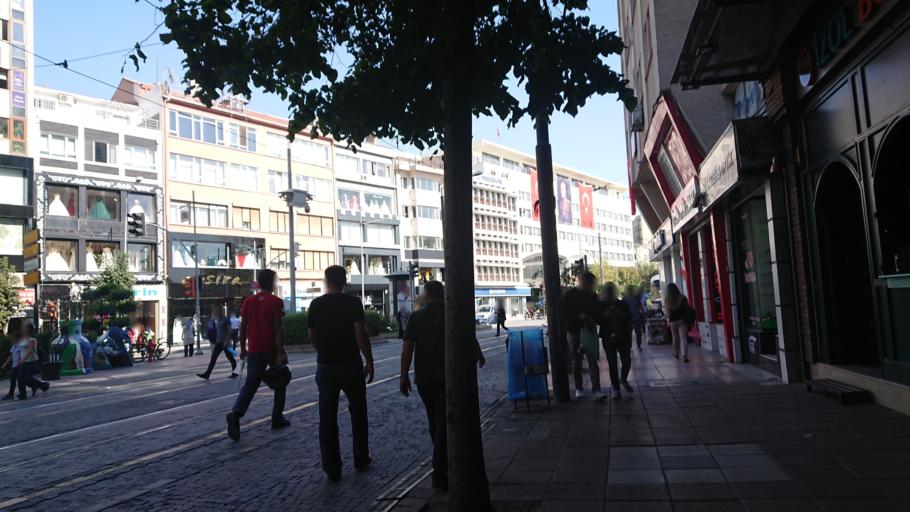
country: TR
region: Eskisehir
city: Eskisehir
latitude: 39.7773
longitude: 30.5176
